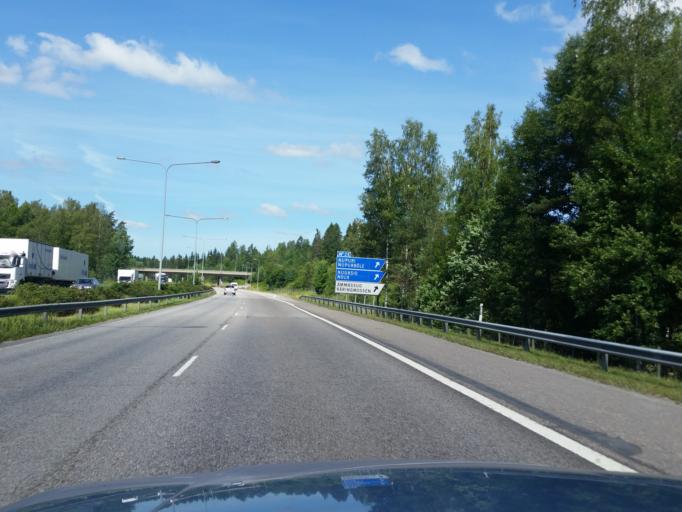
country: FI
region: Uusimaa
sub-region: Helsinki
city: Espoo
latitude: 60.2424
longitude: 24.5724
